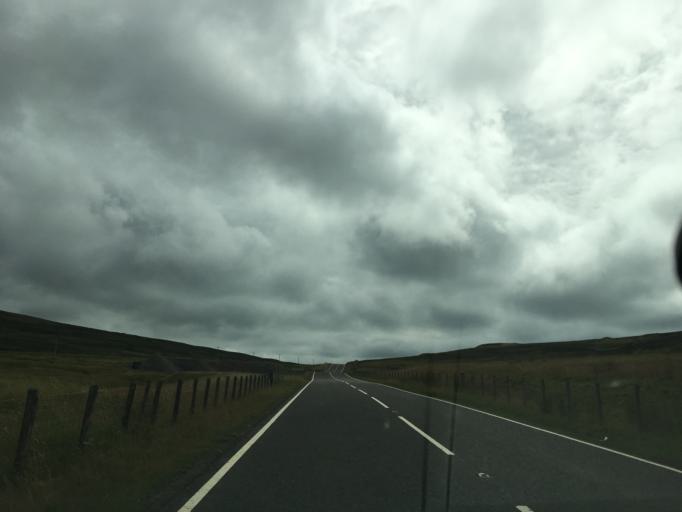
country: GB
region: Scotland
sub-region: Dumfries and Galloway
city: Sanquhar
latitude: 55.4090
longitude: -3.7667
